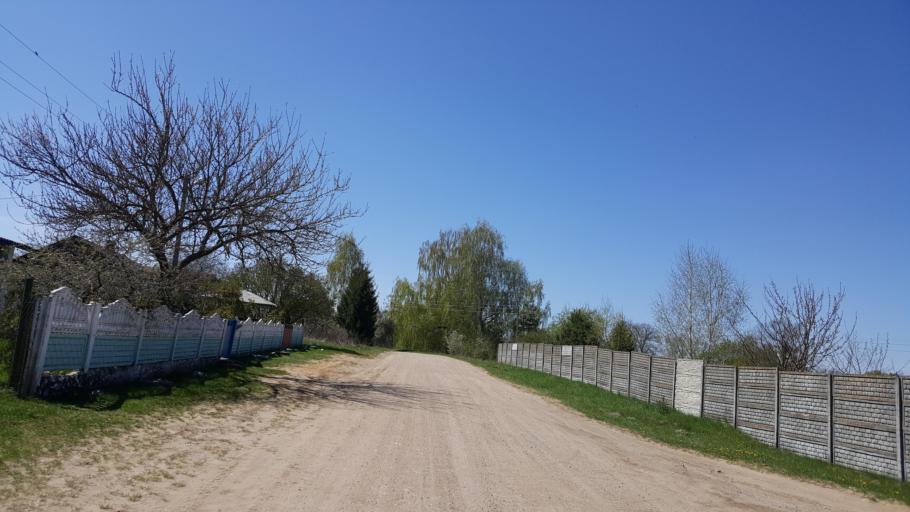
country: BY
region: Brest
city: Charnawchytsy
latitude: 52.3270
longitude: 23.6601
